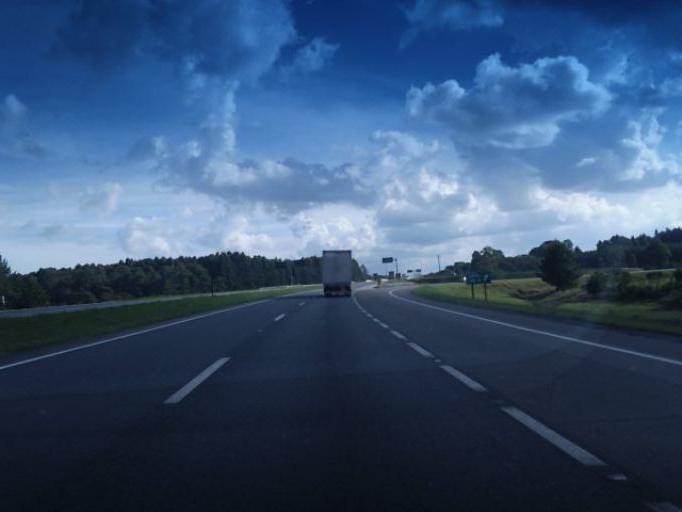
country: BR
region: Parana
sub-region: Piraquara
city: Piraquara
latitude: -25.4586
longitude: -49.0880
